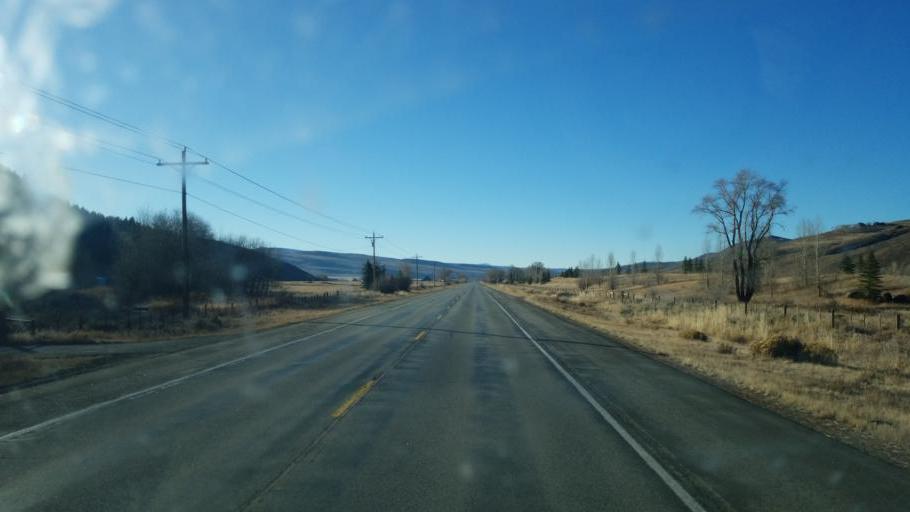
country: US
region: Colorado
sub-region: Gunnison County
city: Crested Butte
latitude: 38.7756
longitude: -106.8683
